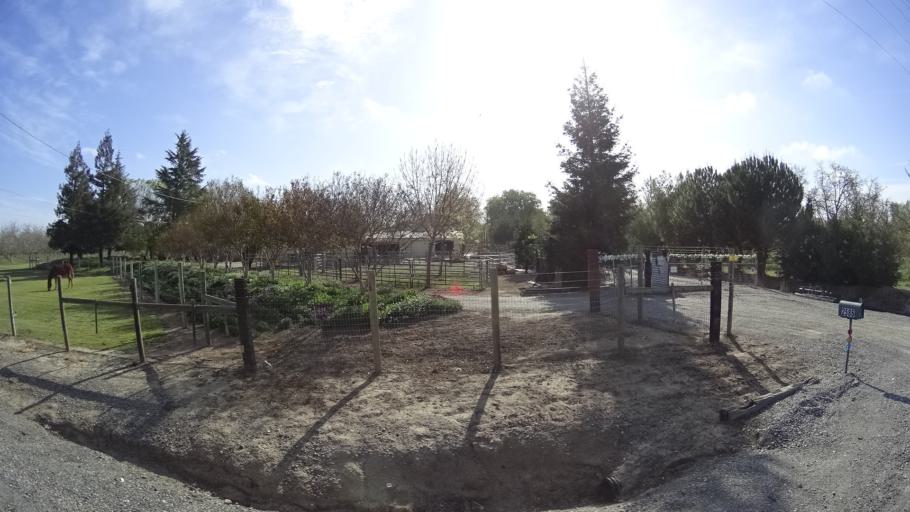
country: US
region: California
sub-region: Glenn County
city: Hamilton City
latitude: 39.5871
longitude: -122.0075
